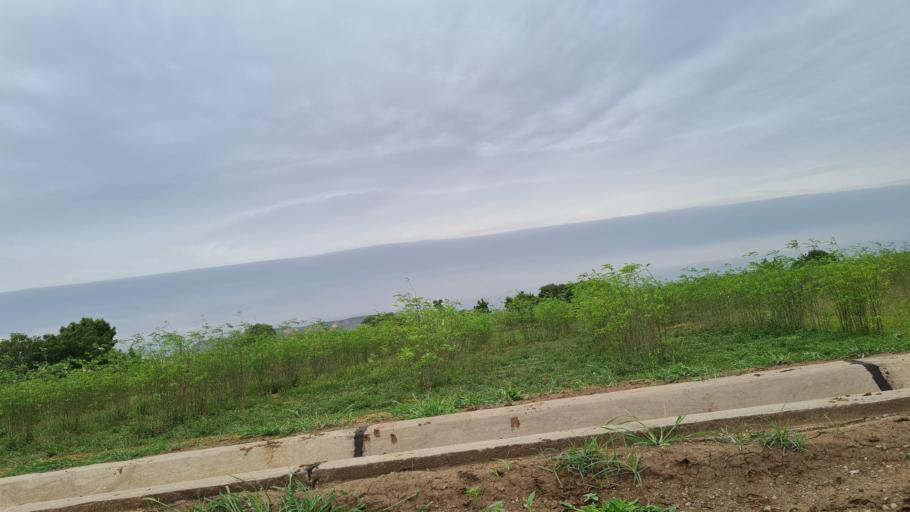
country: NE
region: Tahoua
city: Birni N Konni
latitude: 13.8331
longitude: 5.2662
